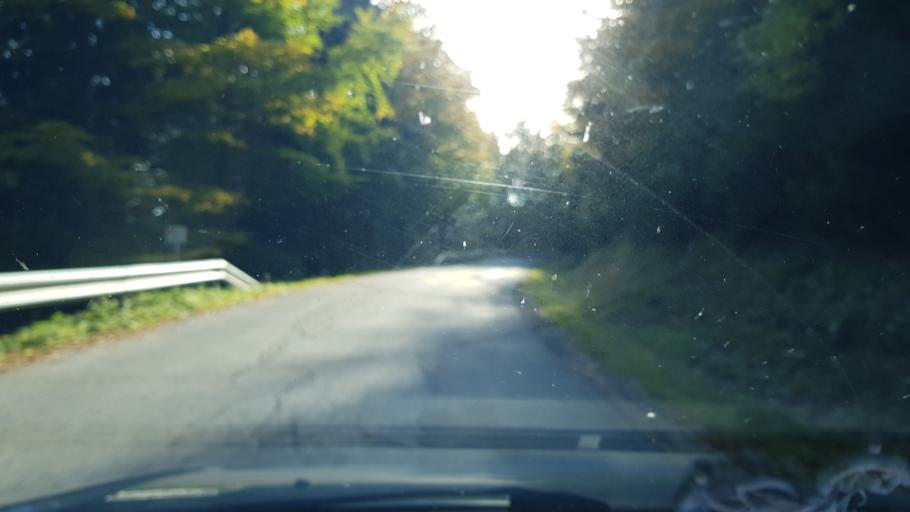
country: SI
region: Slovenj Gradec
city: Legen
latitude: 46.4966
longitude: 15.1920
